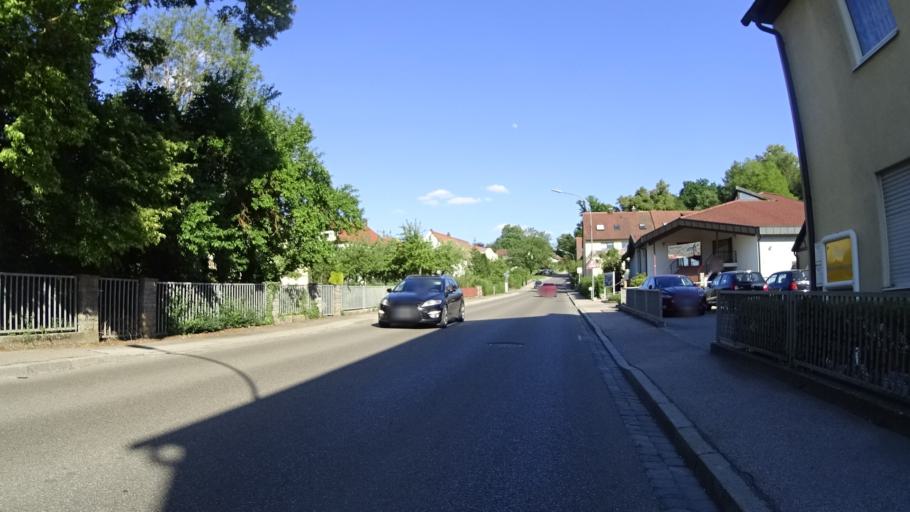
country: DE
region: Bavaria
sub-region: Regierungsbezirk Mittelfranken
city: Feuchtwangen
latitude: 49.1661
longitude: 10.3366
